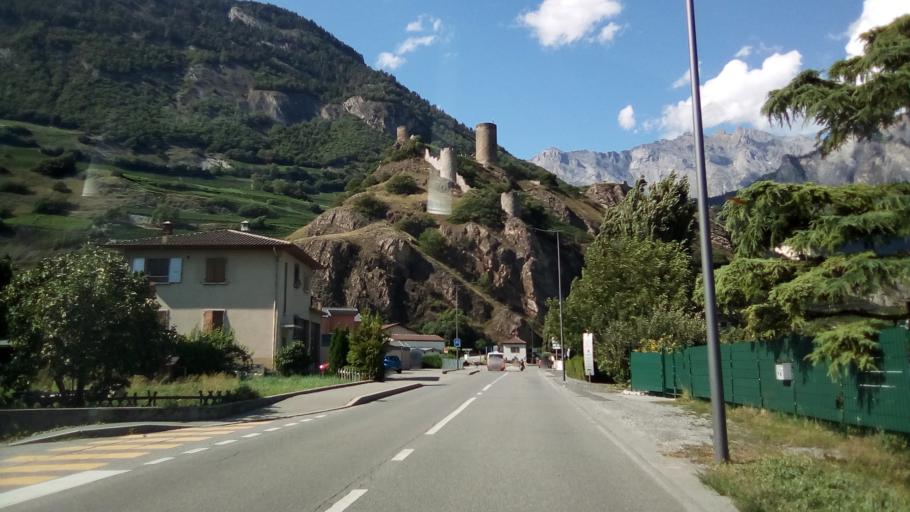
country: CH
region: Valais
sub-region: Martigny District
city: Saillon
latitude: 46.1676
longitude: 7.1833
